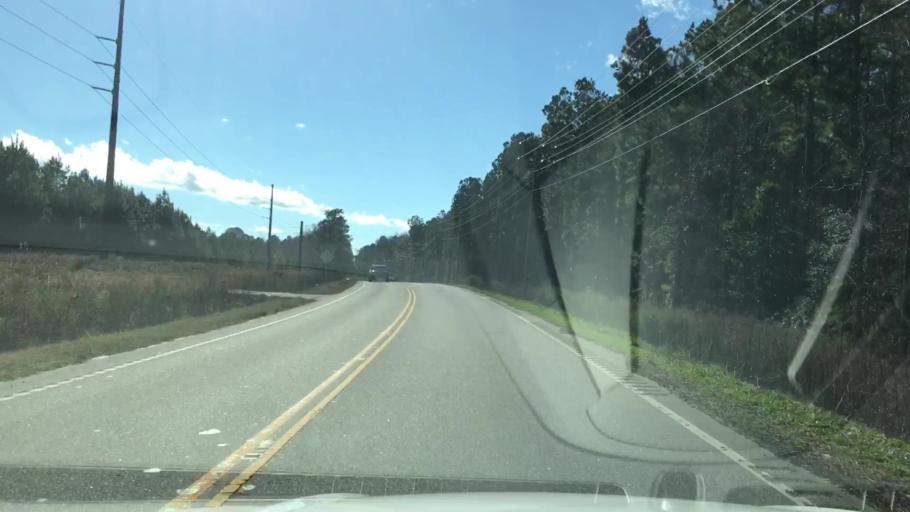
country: US
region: South Carolina
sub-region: Dorchester County
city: Summerville
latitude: 33.0755
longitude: -80.2163
